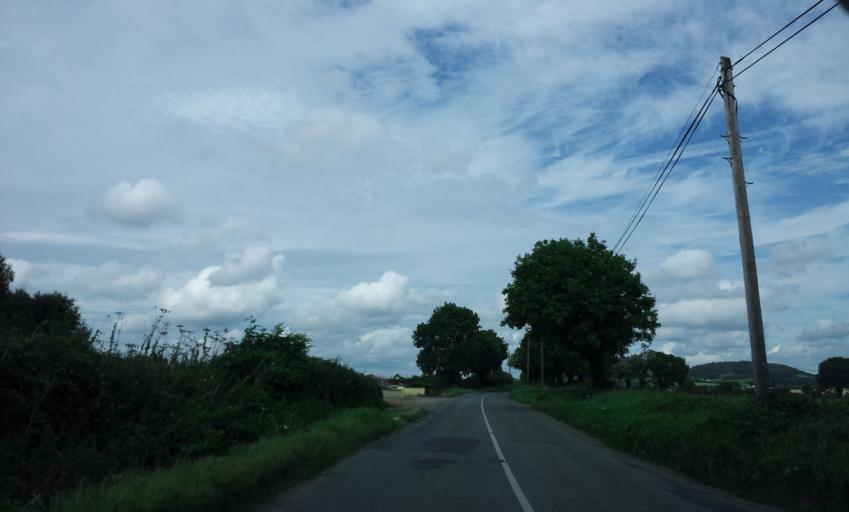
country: IE
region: Leinster
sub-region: Laois
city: Stradbally
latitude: 52.9884
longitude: -7.2194
